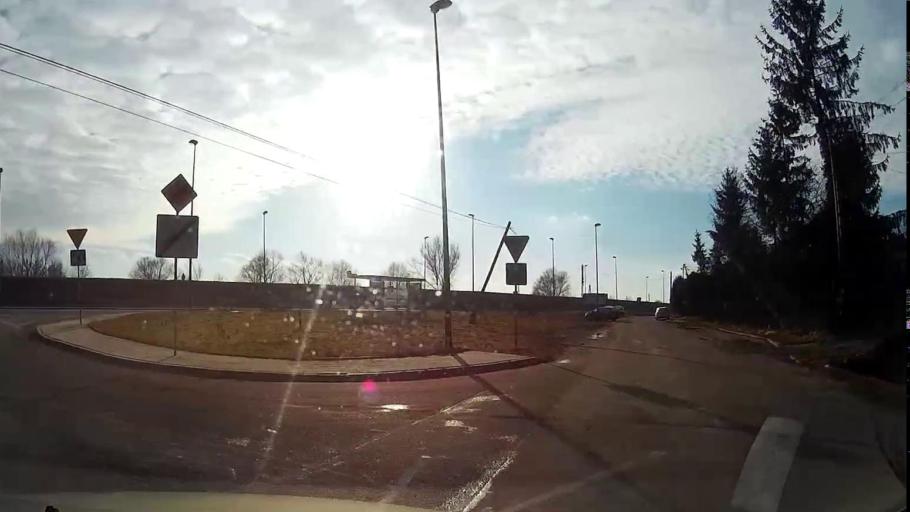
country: PL
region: Lesser Poland Voivodeship
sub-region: Powiat krakowski
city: Rzaska
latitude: 50.0455
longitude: 19.8597
